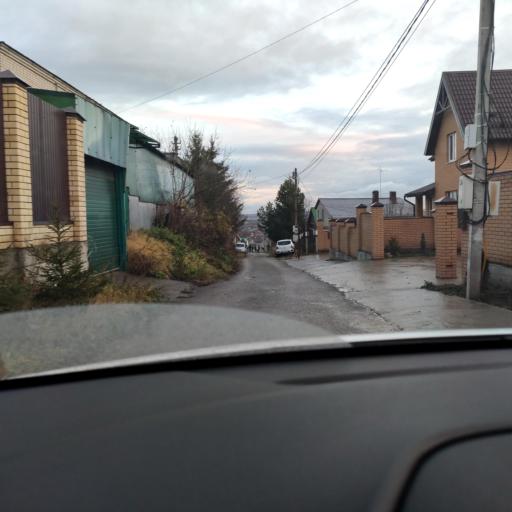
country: RU
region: Tatarstan
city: Stolbishchi
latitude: 55.7545
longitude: 49.2931
